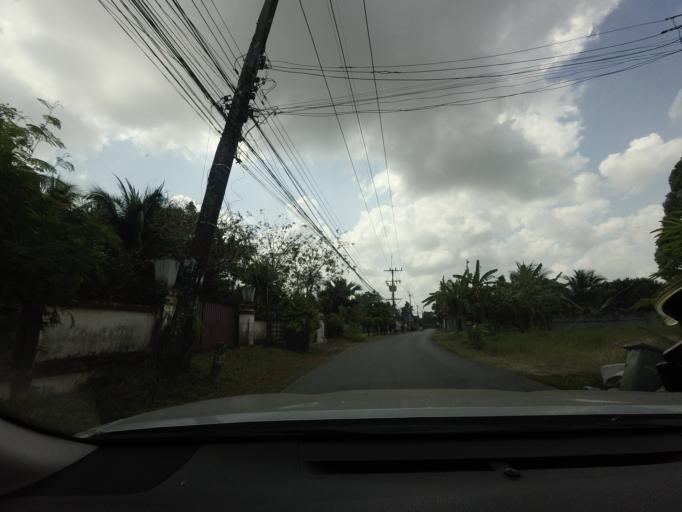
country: TH
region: Nakhon Si Thammarat
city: Nakhon Si Thammarat
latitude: 8.4398
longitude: 99.9298
